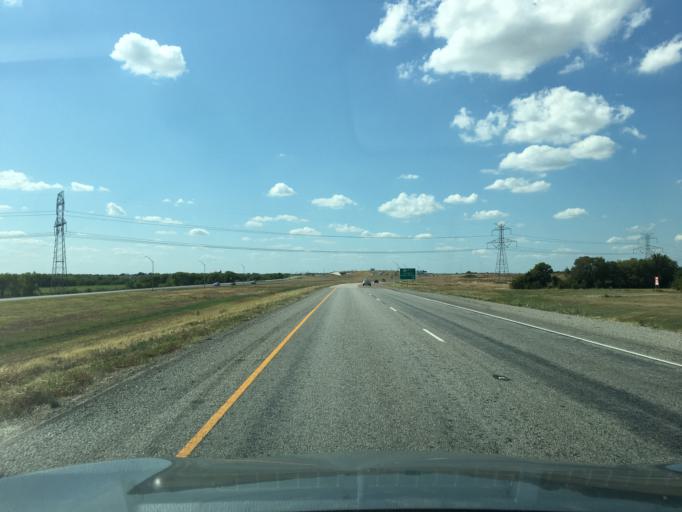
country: US
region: Texas
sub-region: Tarrant County
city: Mansfield
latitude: 32.5171
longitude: -97.0737
